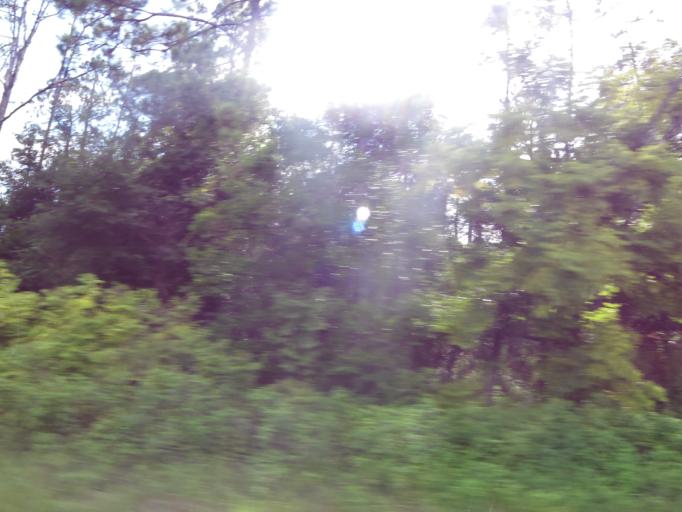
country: US
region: Florida
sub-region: Clay County
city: Green Cove Springs
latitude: 29.9388
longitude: -81.6912
